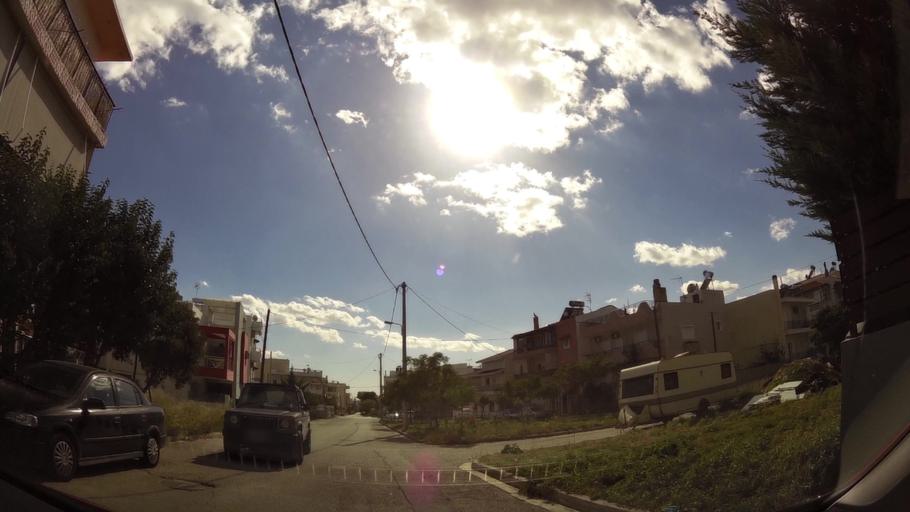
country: GR
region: Attica
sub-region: Nomarchia Anatolikis Attikis
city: Acharnes
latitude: 38.0985
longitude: 23.7322
